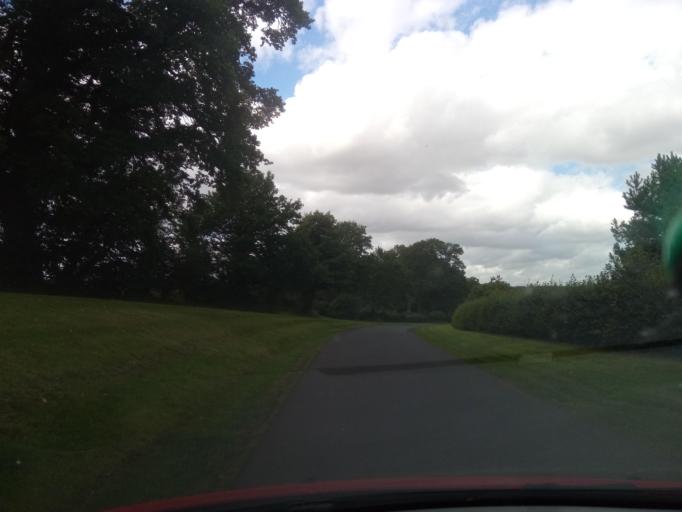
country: GB
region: Scotland
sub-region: The Scottish Borders
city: Coldstream
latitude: 55.6523
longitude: -2.2726
